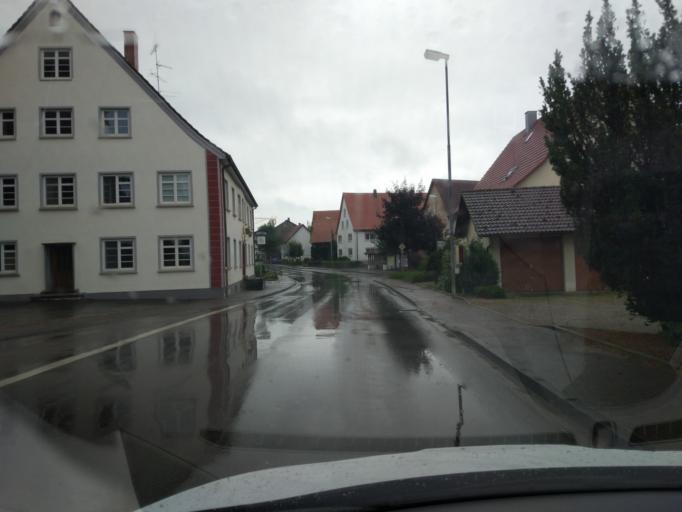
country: DE
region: Baden-Wuerttemberg
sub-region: Tuebingen Region
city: Achstetten
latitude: 48.2795
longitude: 9.9061
